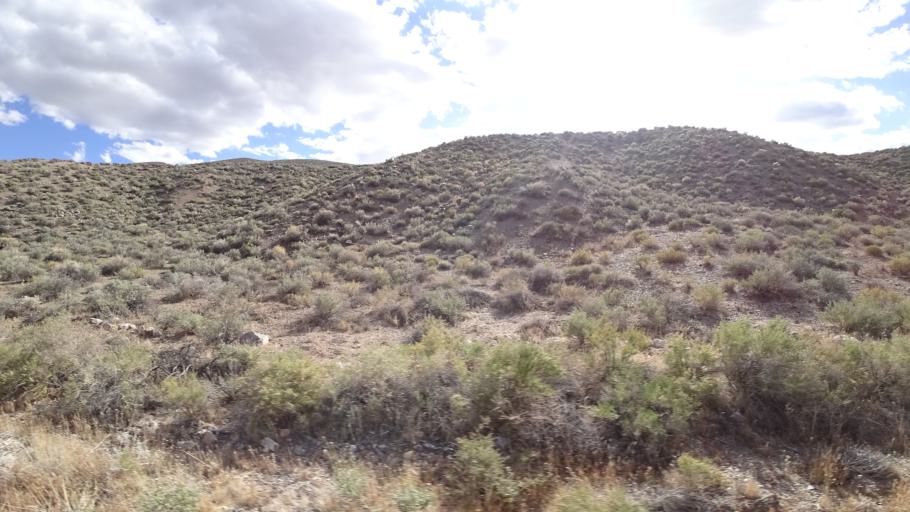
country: US
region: Nevada
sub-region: Nye County
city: Beatty
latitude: 36.4042
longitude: -117.1704
